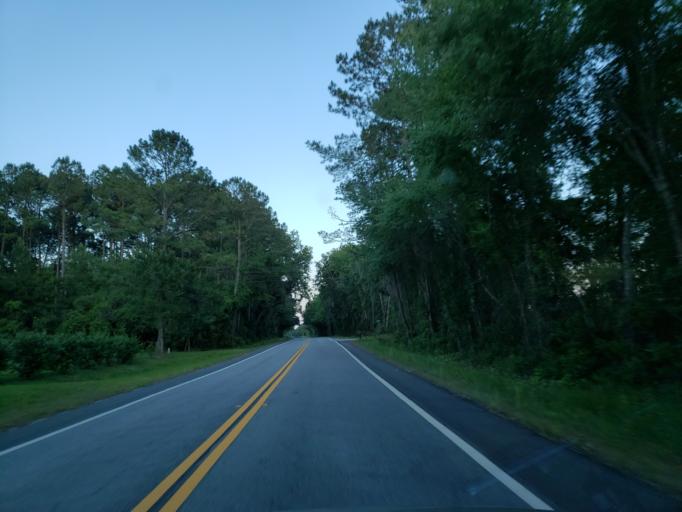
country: US
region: Florida
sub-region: Hamilton County
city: Jasper
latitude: 30.5553
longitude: -83.0781
